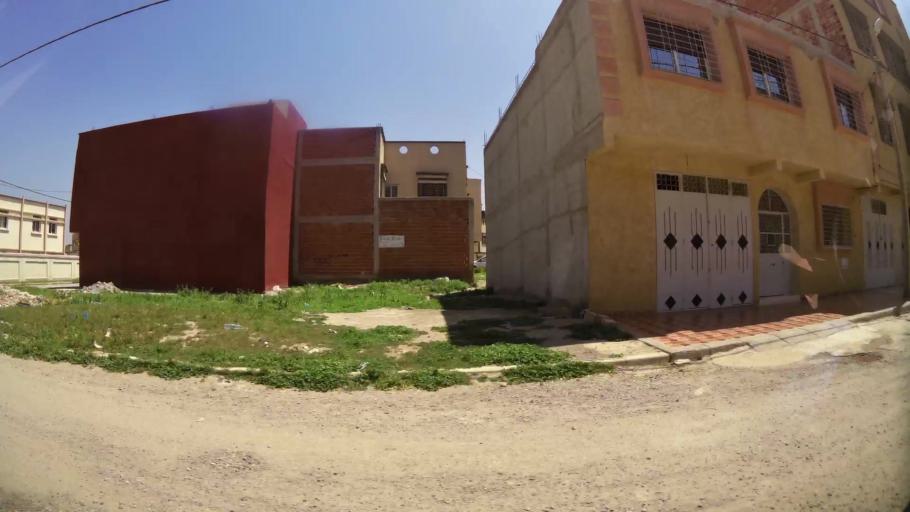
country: MA
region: Oriental
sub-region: Oujda-Angad
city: Oujda
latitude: 34.6982
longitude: -1.8888
